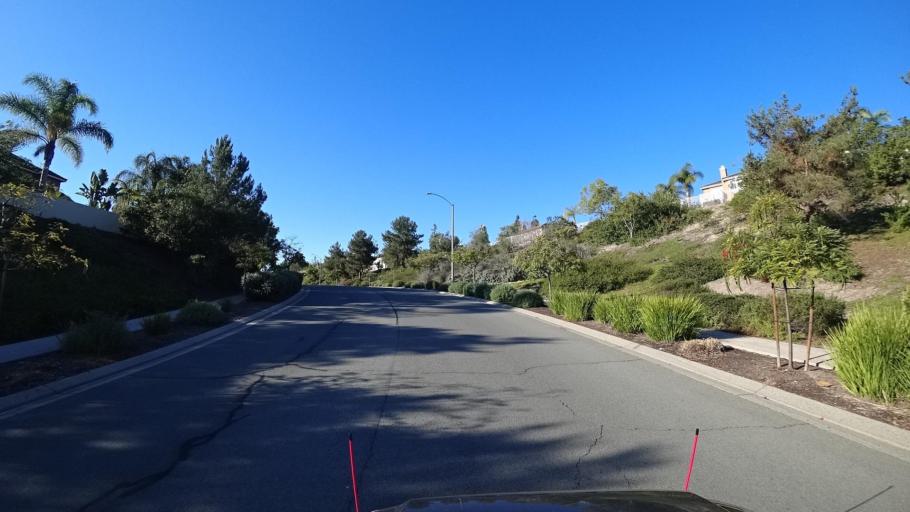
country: US
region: California
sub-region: San Diego County
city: La Presa
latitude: 32.6585
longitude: -116.9449
